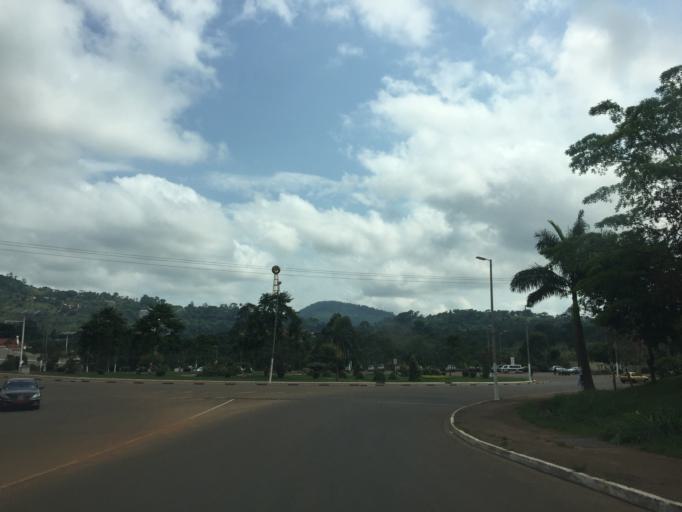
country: CM
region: Centre
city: Yaounde
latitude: 3.8980
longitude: 11.5055
